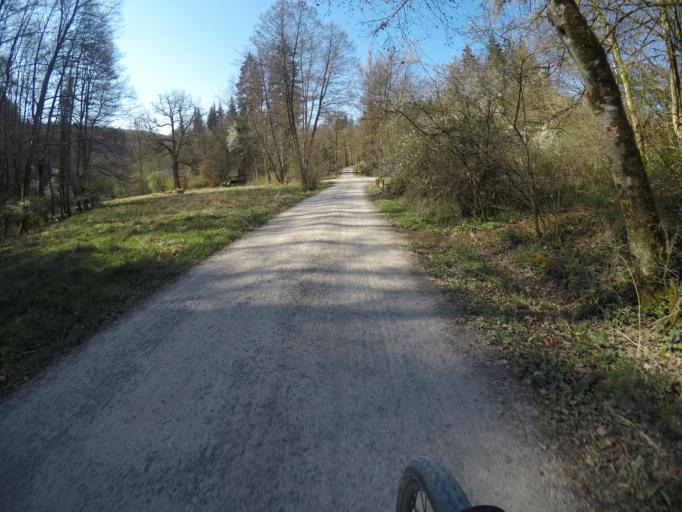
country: DE
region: Baden-Wuerttemberg
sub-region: Regierungsbezirk Stuttgart
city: Weil im Schonbuch
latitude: 48.5770
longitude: 9.0345
